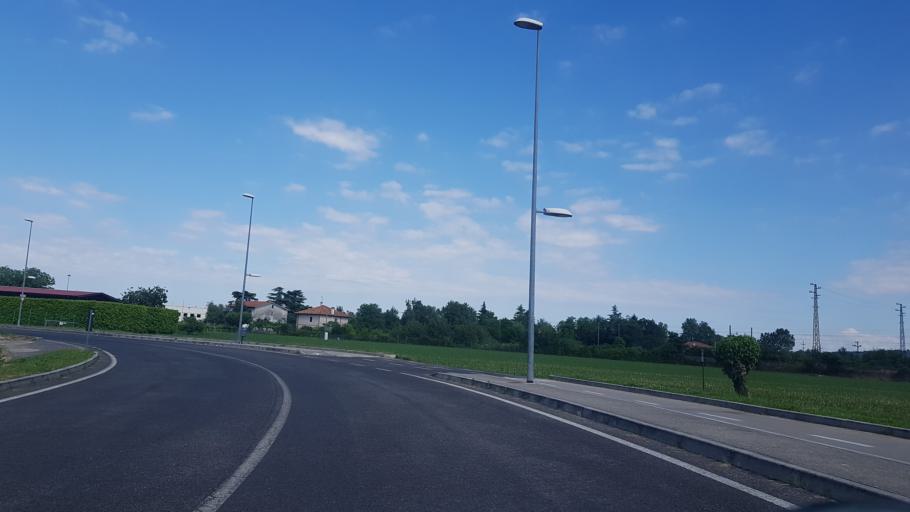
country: IT
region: Friuli Venezia Giulia
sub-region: Provincia di Gorizia
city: Ronchi dei Legionari
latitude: 45.8177
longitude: 13.5173
